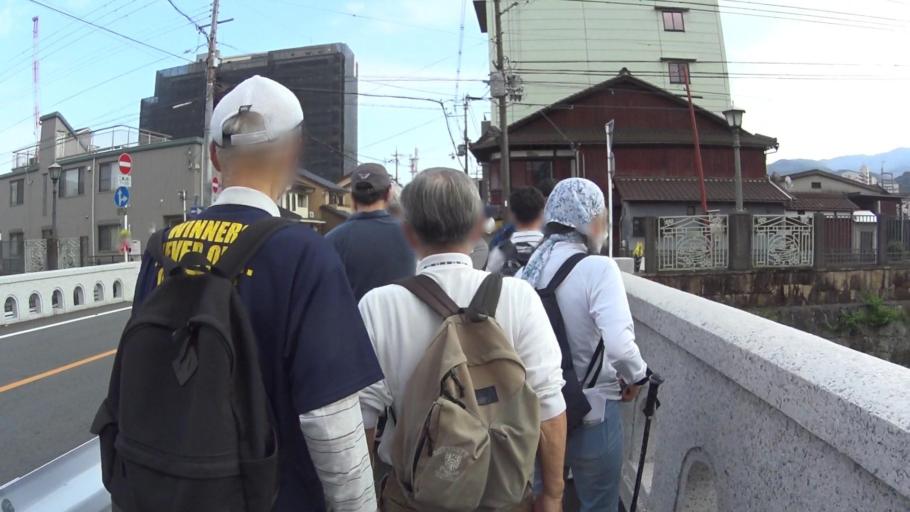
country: JP
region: Osaka
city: Izumiotsu
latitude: 34.5177
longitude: 135.3503
